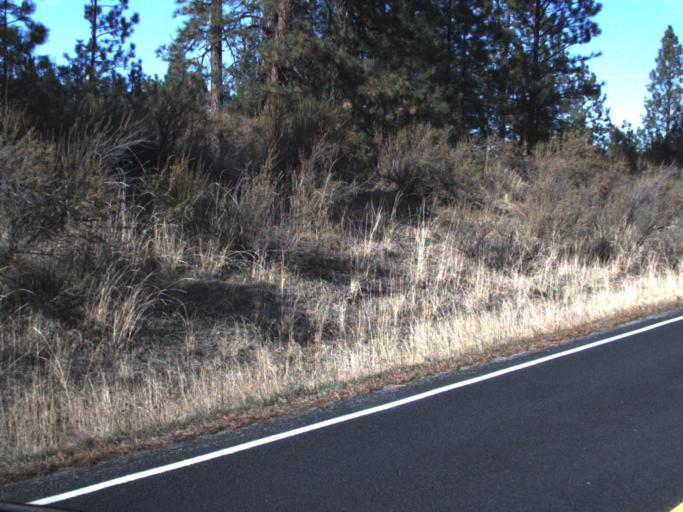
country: US
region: Washington
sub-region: Lincoln County
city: Davenport
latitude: 47.9153
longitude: -118.3315
